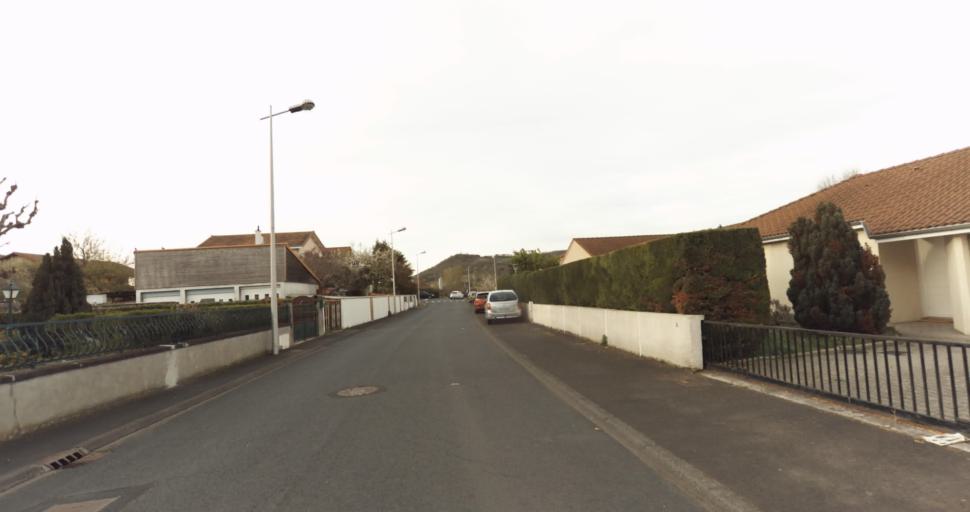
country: FR
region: Auvergne
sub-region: Departement du Puy-de-Dome
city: Cebazat
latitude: 45.8363
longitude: 3.0966
